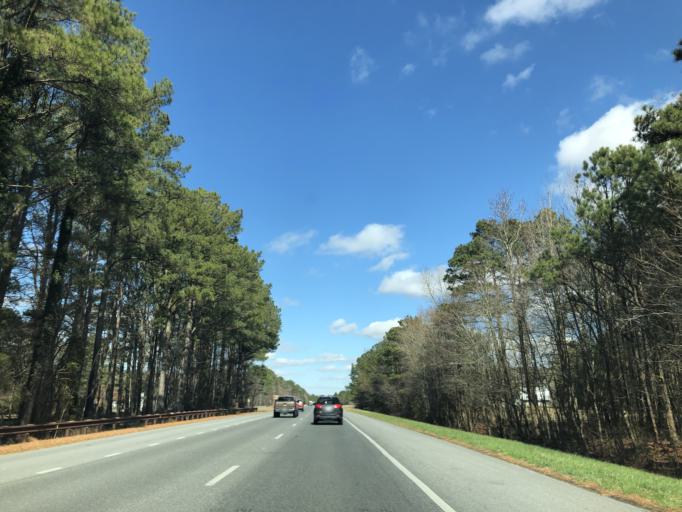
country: US
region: Maryland
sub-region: Worcester County
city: Berlin
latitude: 38.3527
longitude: -75.2142
